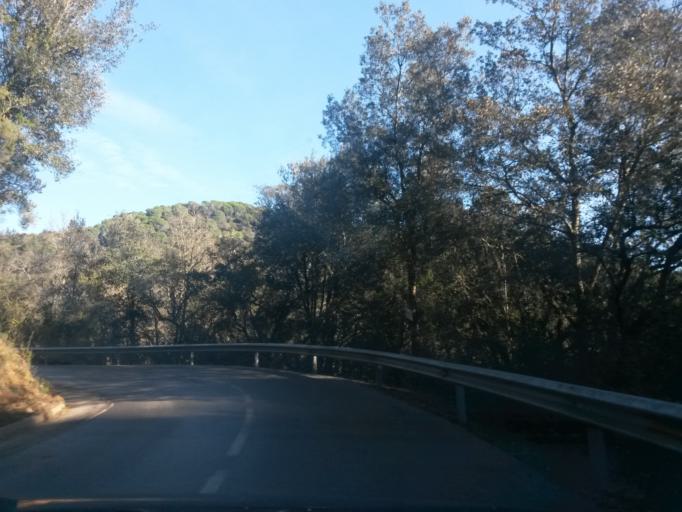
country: ES
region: Catalonia
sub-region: Provincia de Girona
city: Angles
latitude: 41.9951
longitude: 2.6718
